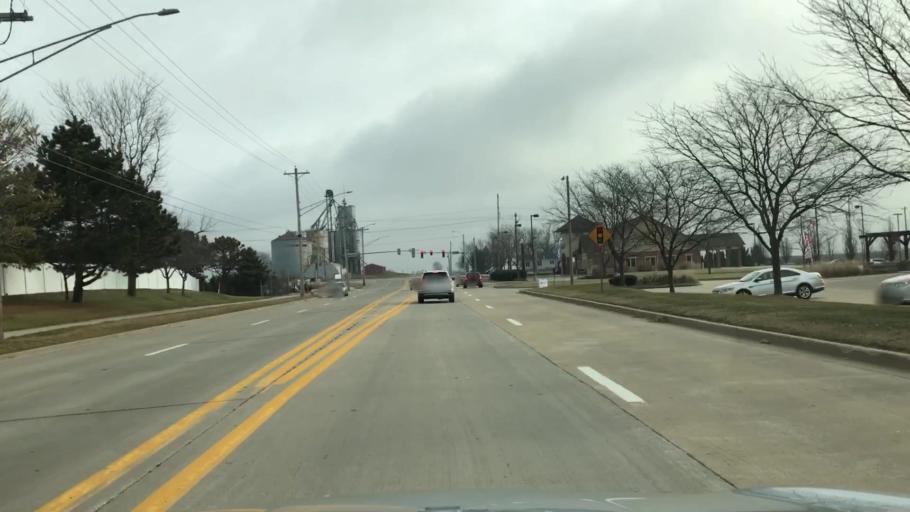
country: US
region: Illinois
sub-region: McLean County
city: Normal
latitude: 40.5026
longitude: -88.9057
